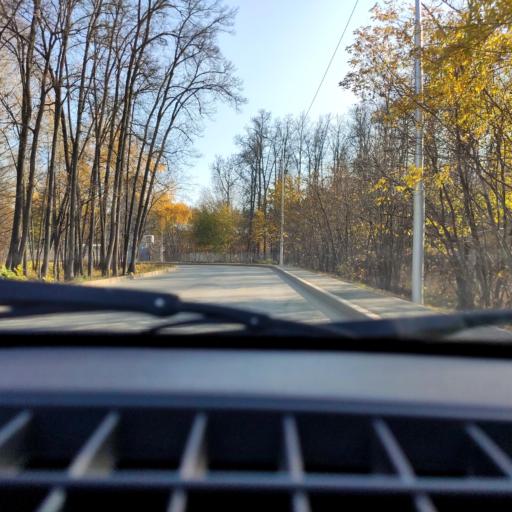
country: RU
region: Bashkortostan
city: Ufa
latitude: 54.7372
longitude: 56.0233
